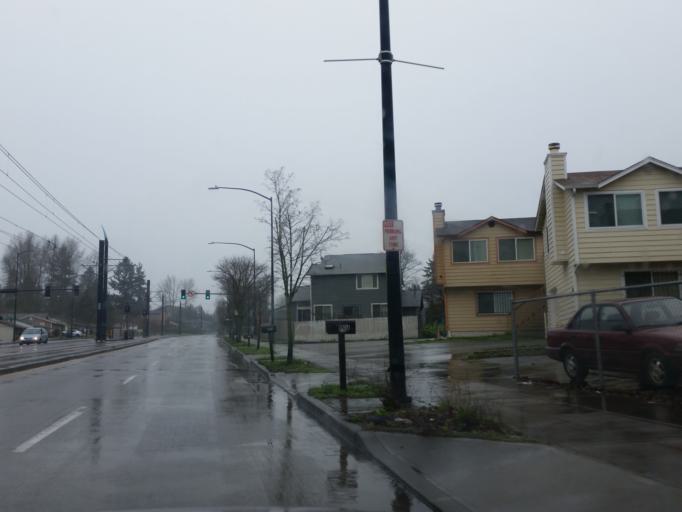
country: US
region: Washington
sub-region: King County
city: Riverton
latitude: 47.5270
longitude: -122.2795
